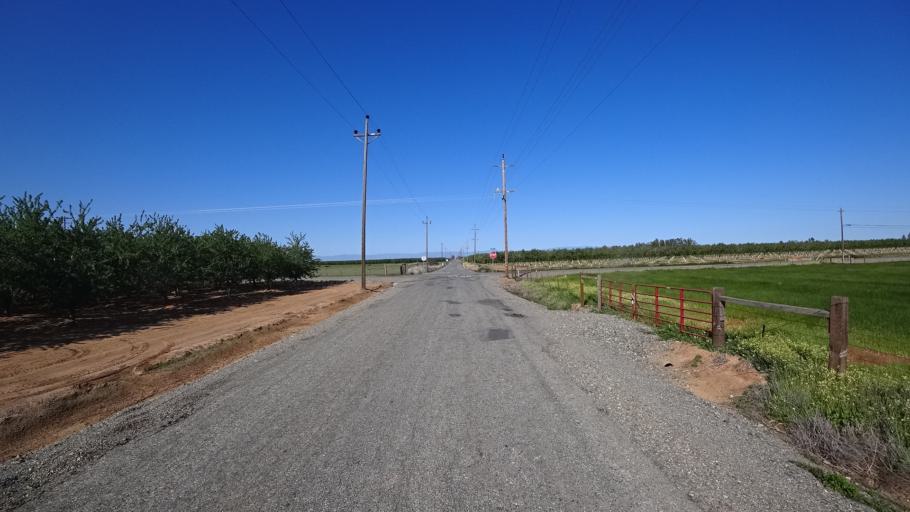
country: US
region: California
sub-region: Glenn County
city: Hamilton City
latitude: 39.7756
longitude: -122.0660
